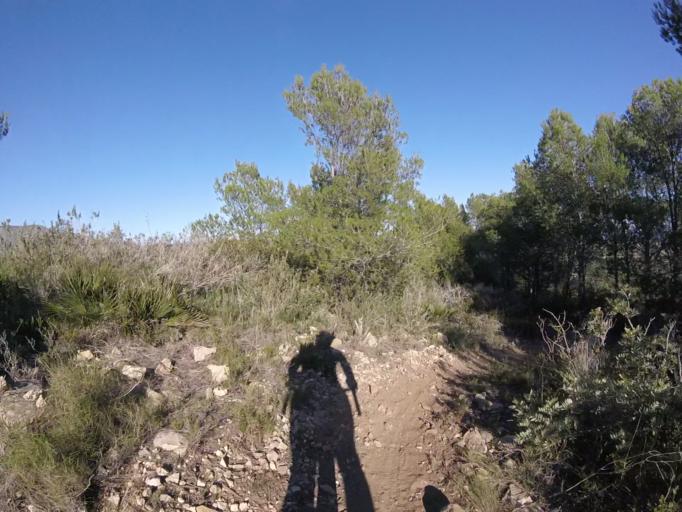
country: ES
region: Valencia
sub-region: Provincia de Castello
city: Orpesa/Oropesa del Mar
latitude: 40.1128
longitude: 0.1169
